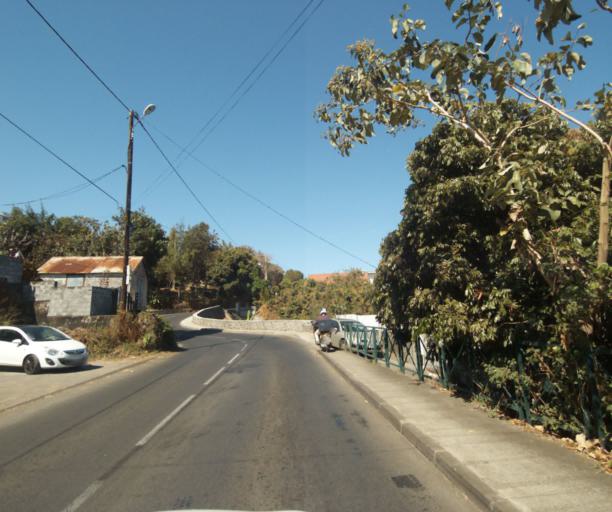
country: RE
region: Reunion
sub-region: Reunion
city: Saint-Paul
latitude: -20.9947
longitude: 55.3305
